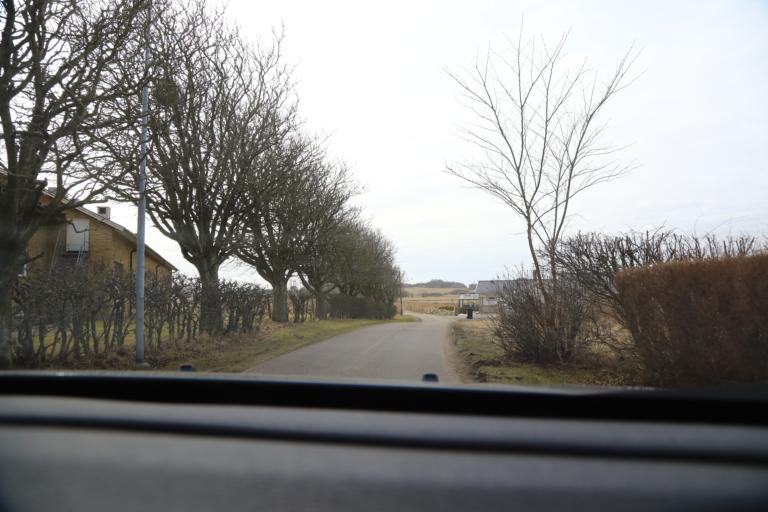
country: SE
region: Halland
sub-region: Kungsbacka Kommun
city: Frillesas
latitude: 57.2334
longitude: 12.1444
